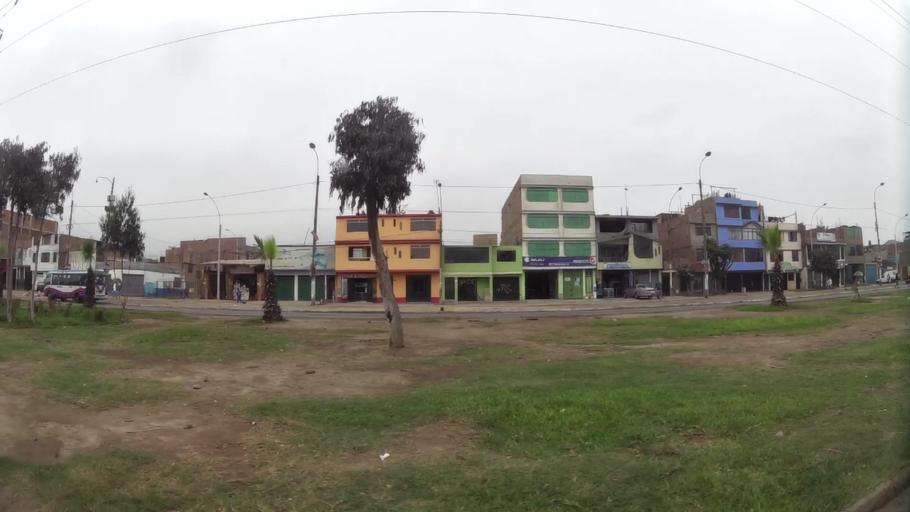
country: PE
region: Lima
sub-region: Lima
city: Independencia
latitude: -11.9879
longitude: -77.0807
